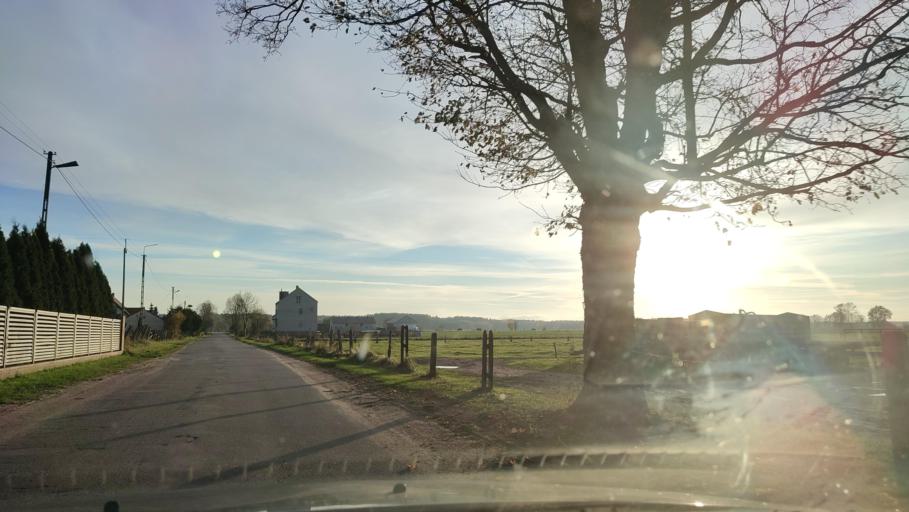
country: PL
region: Masovian Voivodeship
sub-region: Powiat mlawski
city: Dzierzgowo
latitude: 53.3118
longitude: 20.6720
